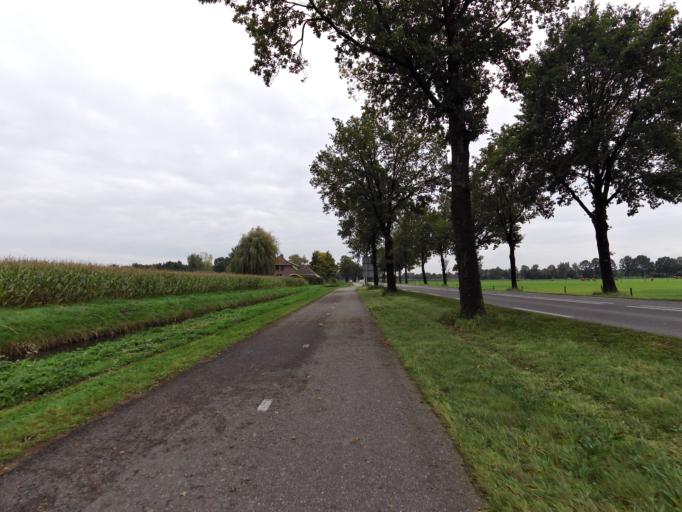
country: NL
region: Gelderland
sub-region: Oude IJsselstreek
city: Gendringen
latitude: 51.8958
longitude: 6.3593
